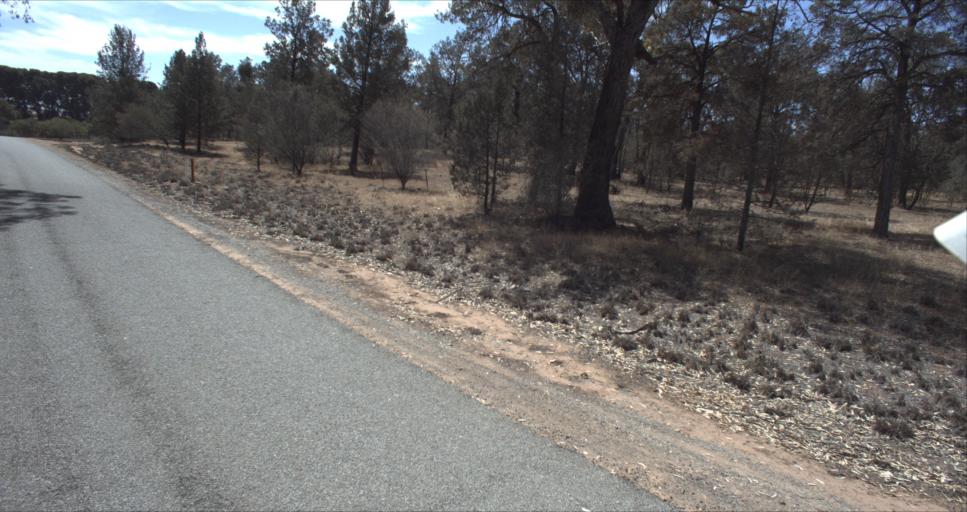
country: AU
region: New South Wales
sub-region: Leeton
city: Leeton
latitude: -34.6716
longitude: 146.4440
